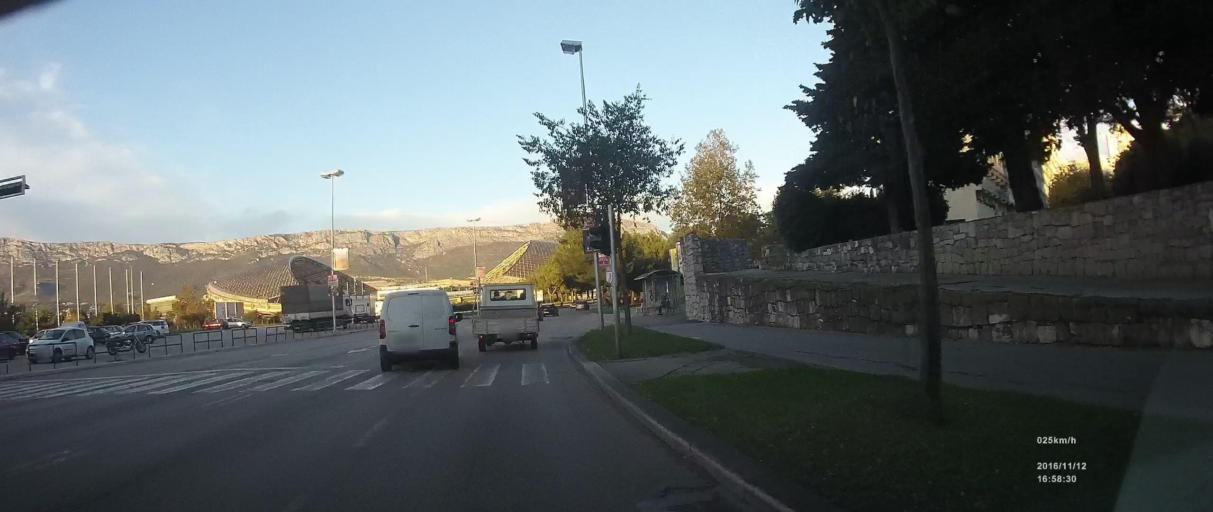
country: HR
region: Splitsko-Dalmatinska
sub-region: Grad Split
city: Split
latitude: 43.5165
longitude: 16.4300
